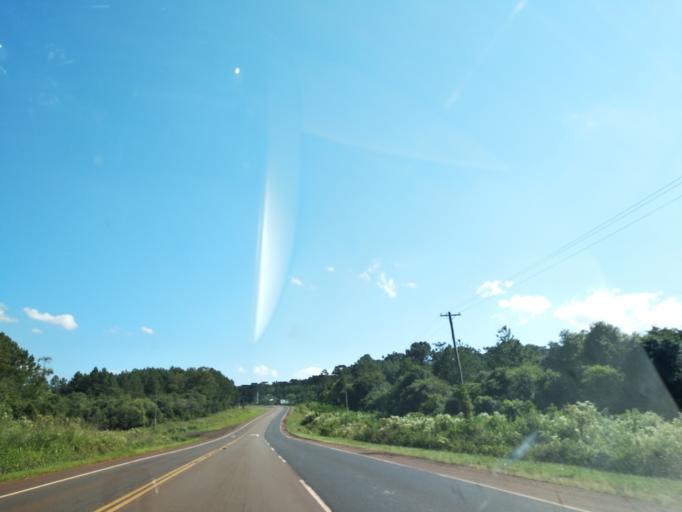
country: AR
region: Misiones
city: Puerto Piray
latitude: -26.4893
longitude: -54.6704
